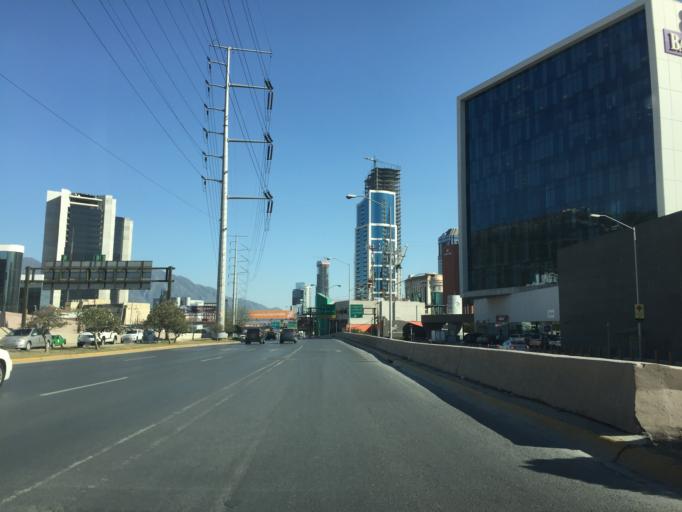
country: MX
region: Nuevo Leon
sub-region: Monterrey
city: Monterrey
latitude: 25.6536
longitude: -100.3376
